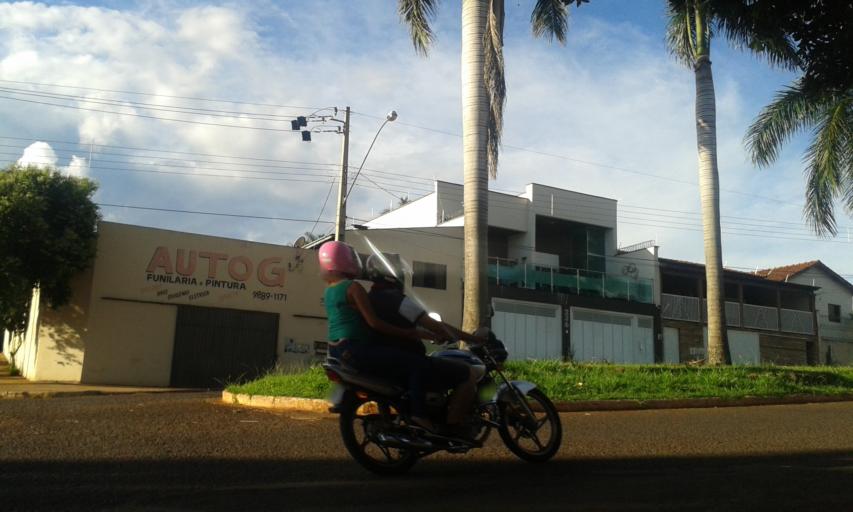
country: BR
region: Minas Gerais
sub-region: Ituiutaba
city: Ituiutaba
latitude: -18.9617
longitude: -49.4603
